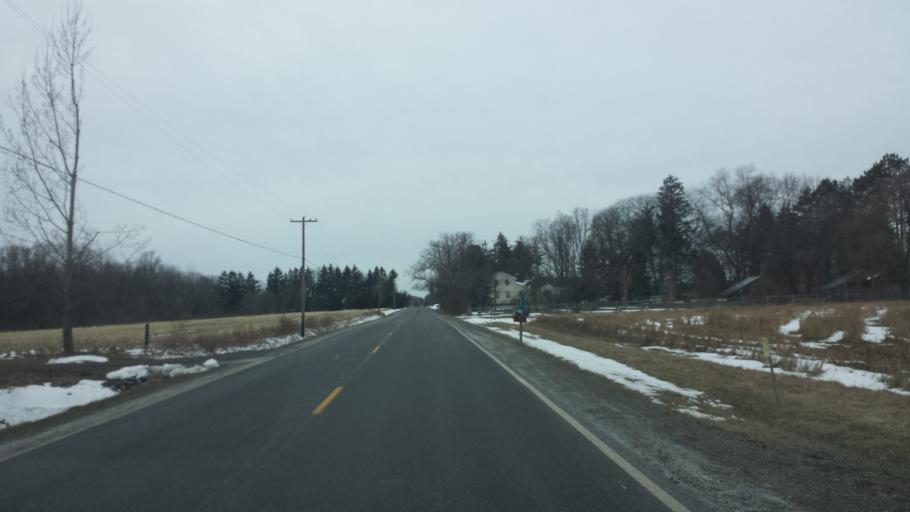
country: US
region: New York
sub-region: Tompkins County
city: Northwest Ithaca
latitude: 42.4963
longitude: -76.5831
